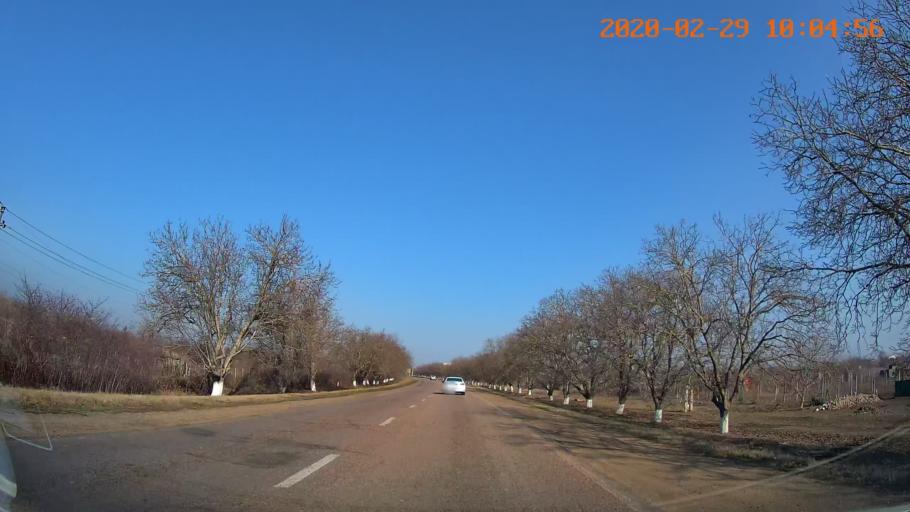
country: MD
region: Telenesti
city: Tiraspolul Nou
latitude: 46.8027
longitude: 29.6737
